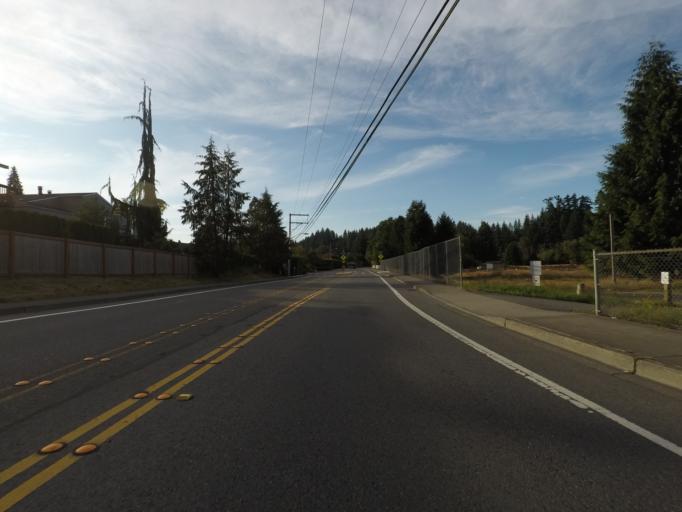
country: US
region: Washington
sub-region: King County
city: Bothell
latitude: 47.7458
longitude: -122.2125
